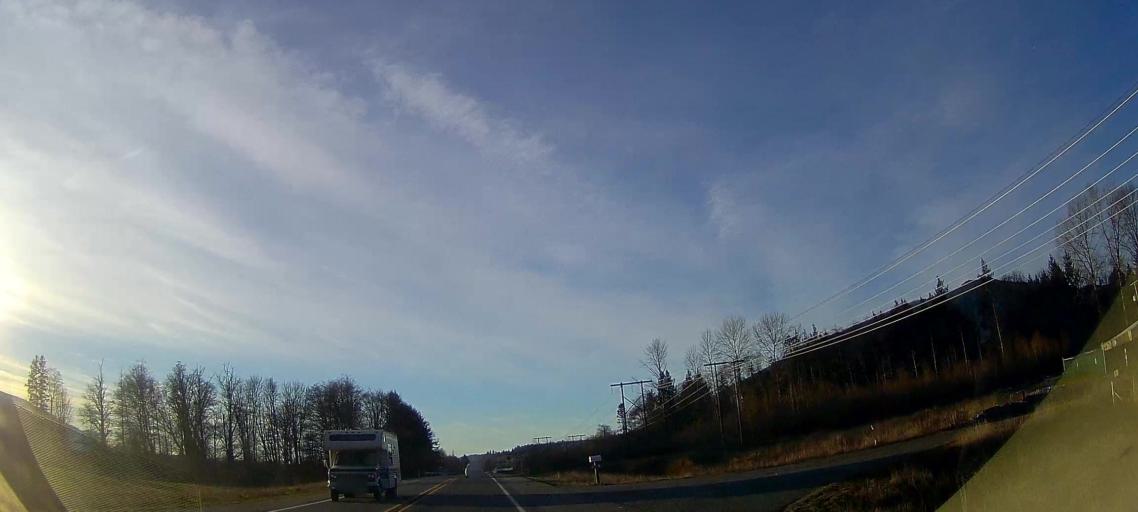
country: US
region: Washington
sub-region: Skagit County
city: Sedro-Woolley
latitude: 48.5296
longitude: -122.0239
